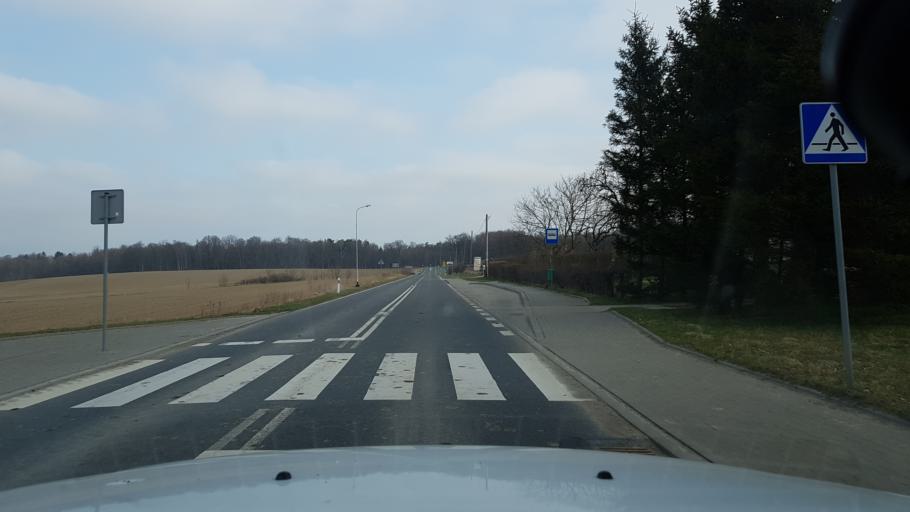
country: PL
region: West Pomeranian Voivodeship
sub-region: Powiat koszalinski
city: Sianow
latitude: 54.2669
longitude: 16.2681
